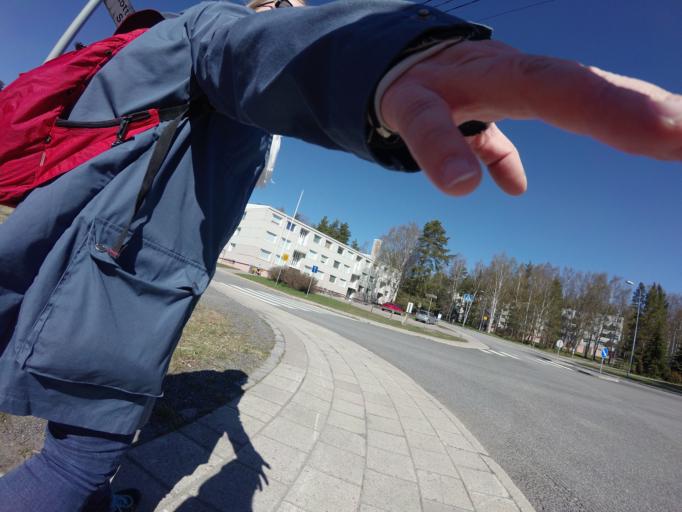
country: FI
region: Varsinais-Suomi
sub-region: Turku
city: Raisio
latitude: 60.4565
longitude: 22.1707
